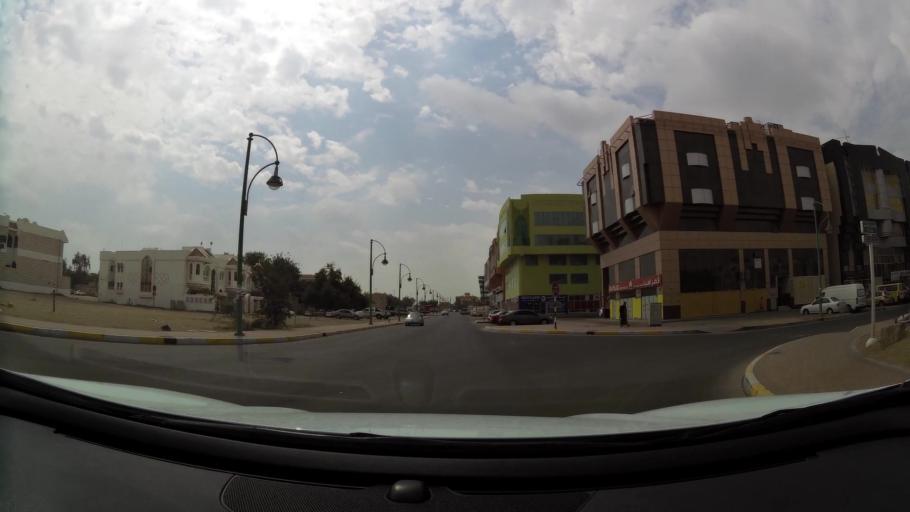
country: OM
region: Al Buraimi
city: Al Buraymi
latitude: 24.2236
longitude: 55.7746
